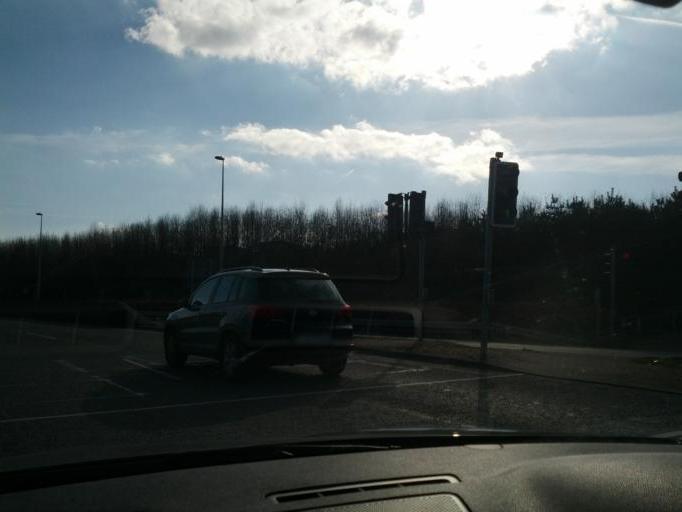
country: IE
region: Leinster
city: Lucan
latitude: 53.3276
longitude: -6.4319
